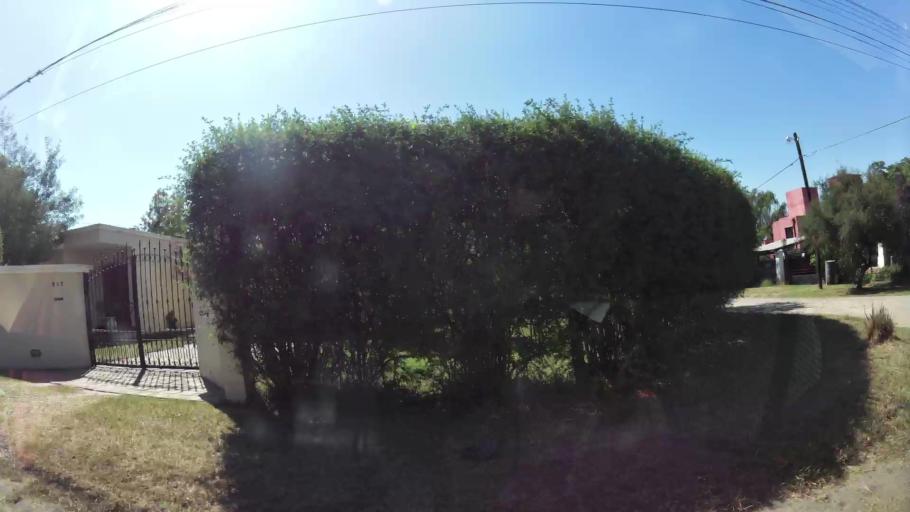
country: AR
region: Cordoba
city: Villa Allende
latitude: -31.2957
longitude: -64.2823
